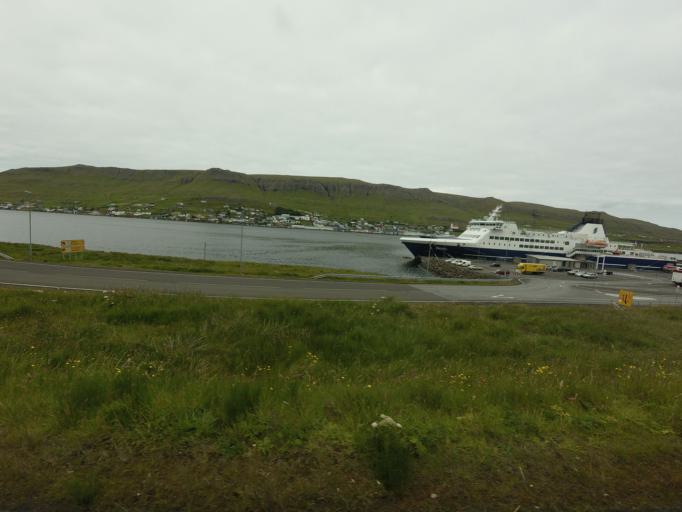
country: FO
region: Suduroy
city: Tvoroyri
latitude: 61.5482
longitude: -6.8214
